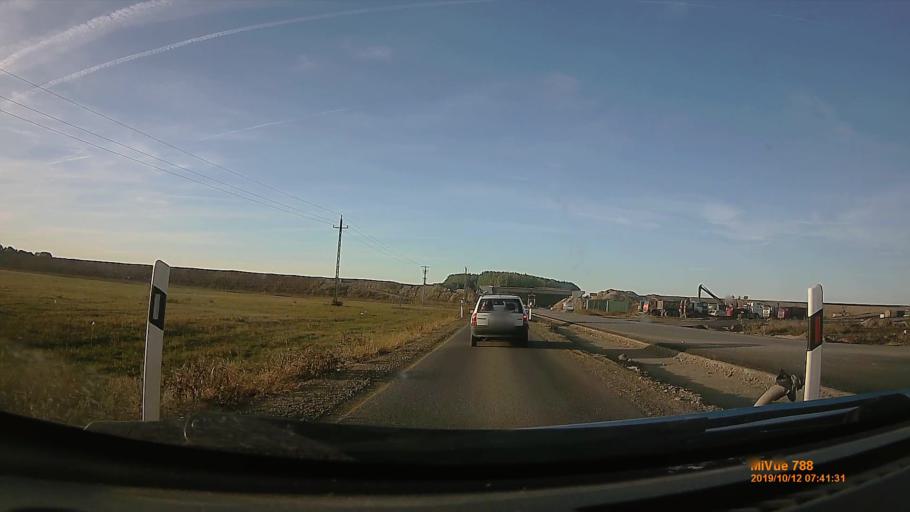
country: HU
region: Hajdu-Bihar
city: Pocsaj
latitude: 47.2058
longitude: 21.7968
